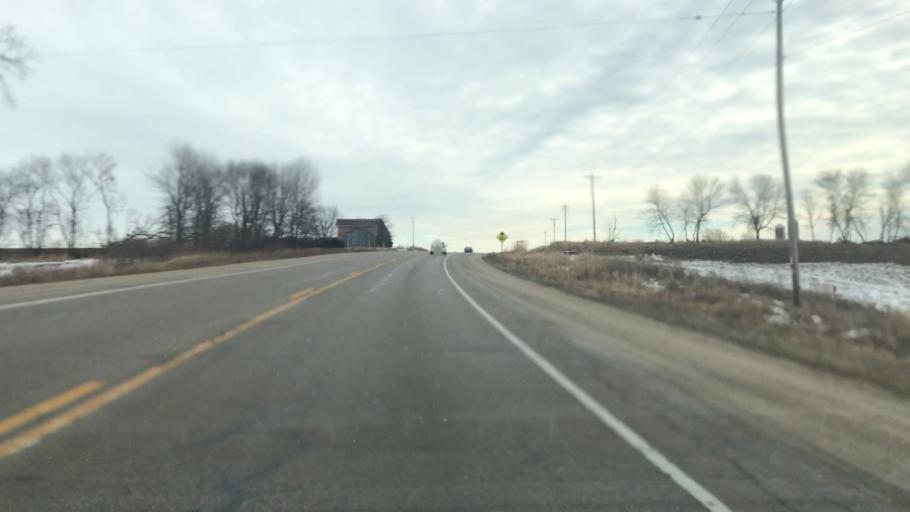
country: US
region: Wisconsin
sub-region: Dodge County
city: Theresa
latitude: 43.4306
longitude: -88.4462
